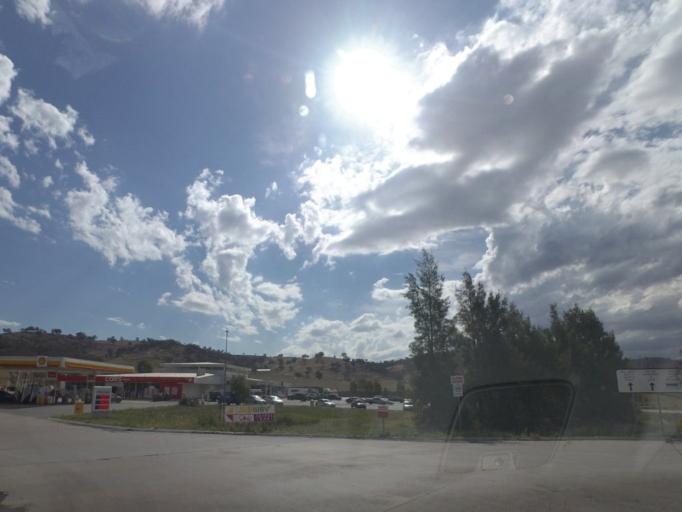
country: AU
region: New South Wales
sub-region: Gundagai
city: Gundagai
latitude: -35.0038
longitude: 148.1116
